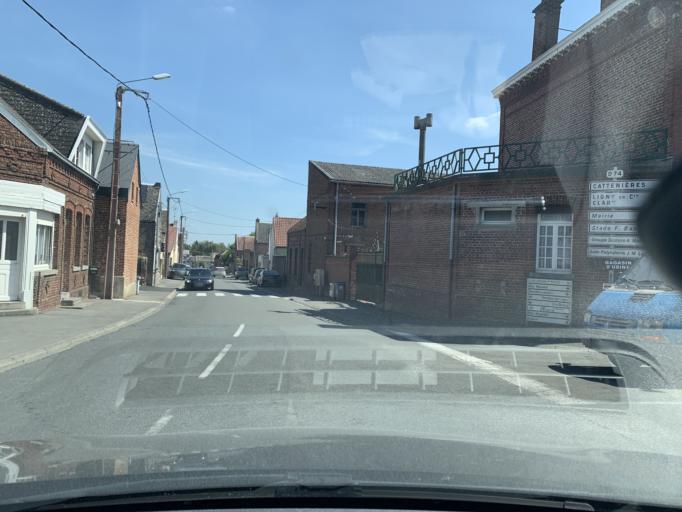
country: FR
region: Nord-Pas-de-Calais
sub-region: Departement du Nord
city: Fontaine-au-Pire
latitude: 50.1326
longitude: 3.3779
